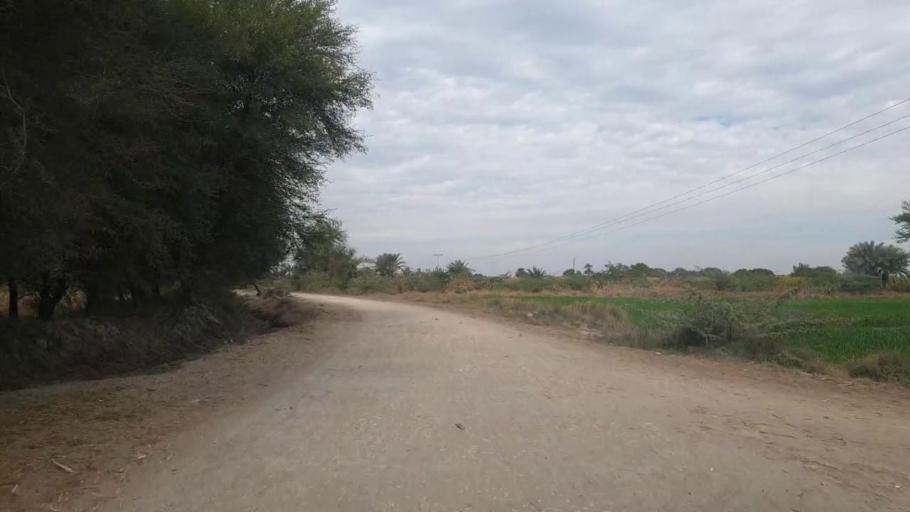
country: PK
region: Sindh
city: Sinjhoro
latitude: 26.0226
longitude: 68.8746
